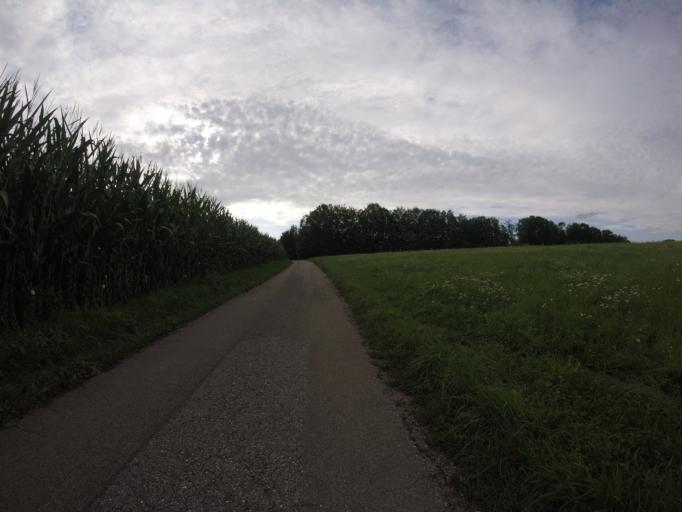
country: DE
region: Baden-Wuerttemberg
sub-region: Regierungsbezirk Stuttgart
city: Backnang
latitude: 48.9414
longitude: 9.4510
